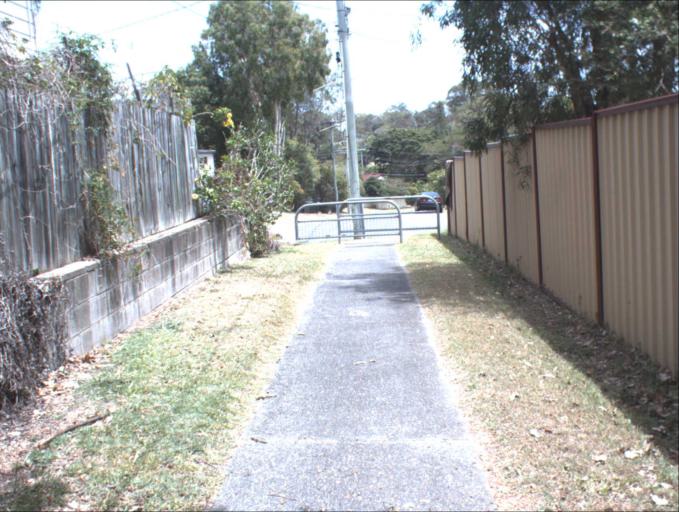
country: AU
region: Queensland
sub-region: Logan
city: Rochedale South
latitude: -27.5919
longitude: 153.1346
